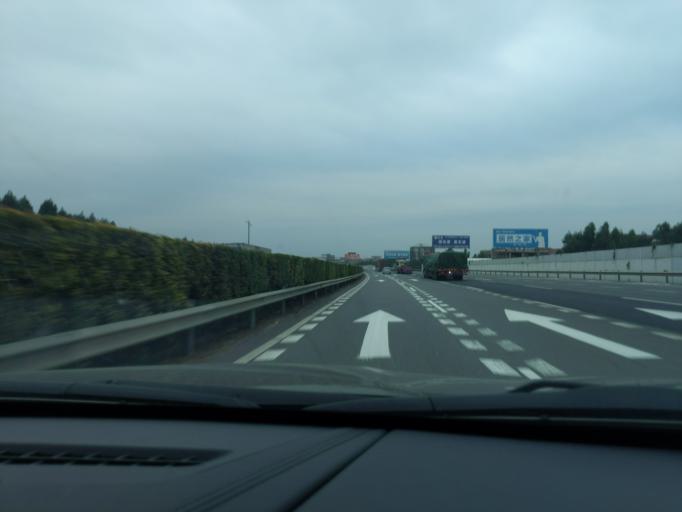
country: CN
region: Fujian
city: Anhai
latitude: 24.7321
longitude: 118.4183
